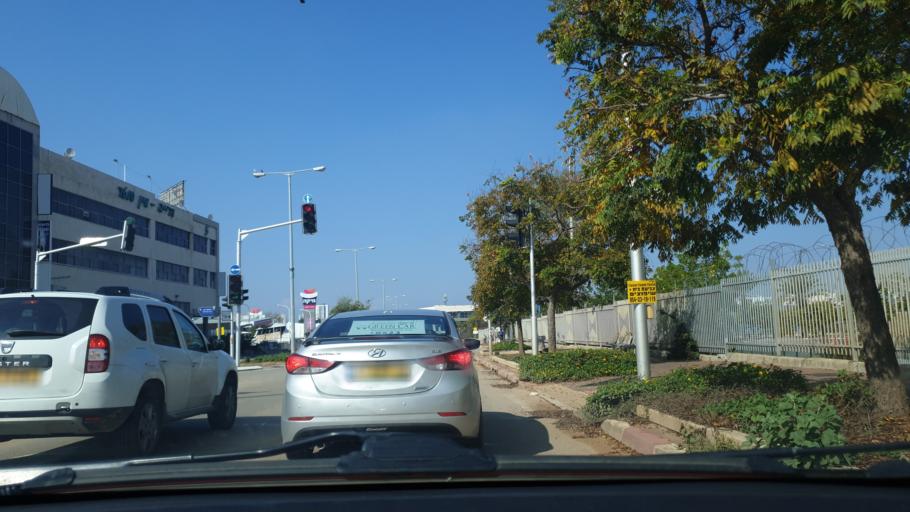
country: IL
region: Central District
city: Bet Dagan
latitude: 31.9752
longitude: 34.8140
